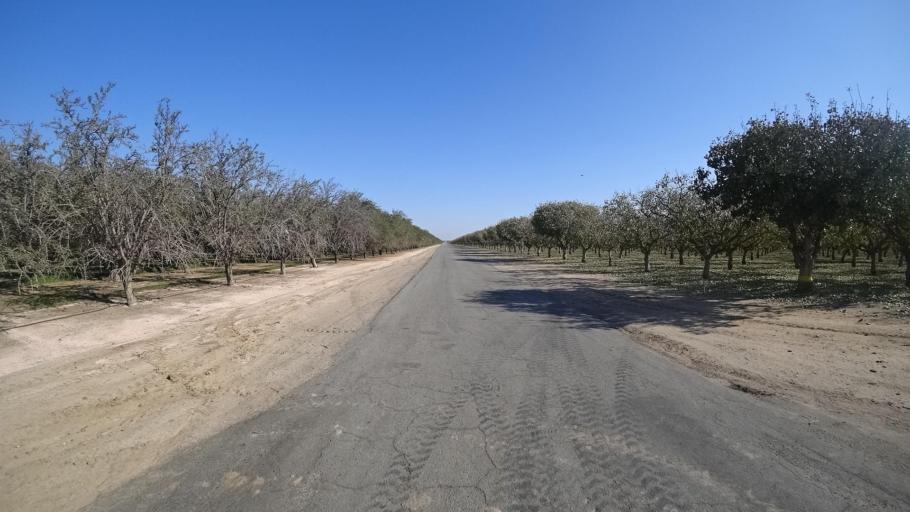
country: US
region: California
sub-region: Kern County
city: McFarland
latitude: 35.6456
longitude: -119.1865
